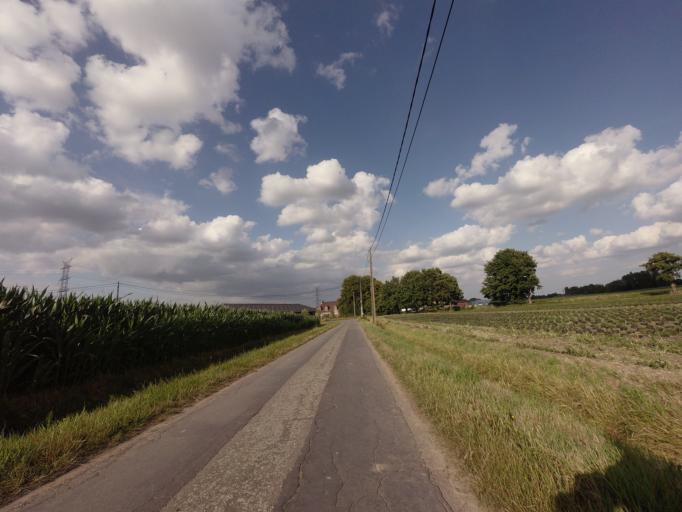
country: BE
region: Flanders
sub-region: Provincie Antwerpen
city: Kontich
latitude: 51.1119
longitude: 4.4665
